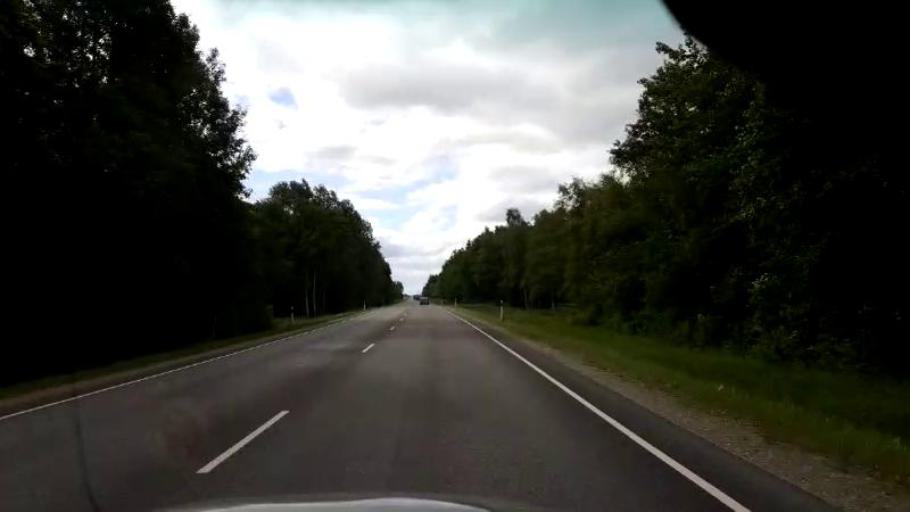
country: EE
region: Paernumaa
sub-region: Halinga vald
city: Parnu-Jaagupi
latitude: 58.6035
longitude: 24.5122
